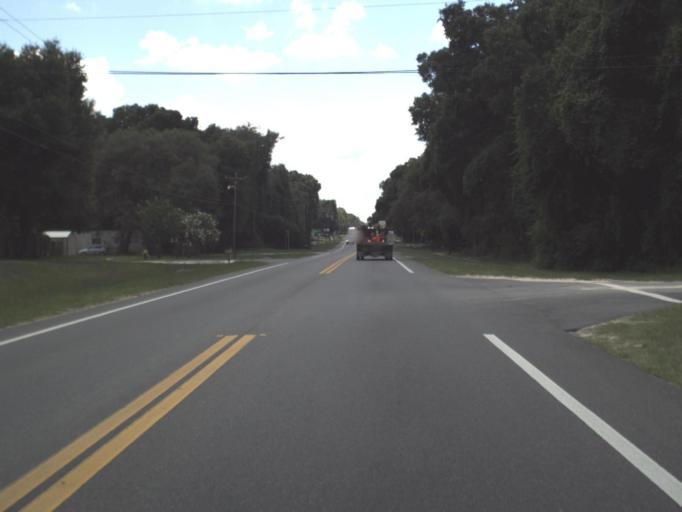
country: US
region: Florida
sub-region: Clay County
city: Keystone Heights
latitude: 29.7743
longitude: -82.0142
